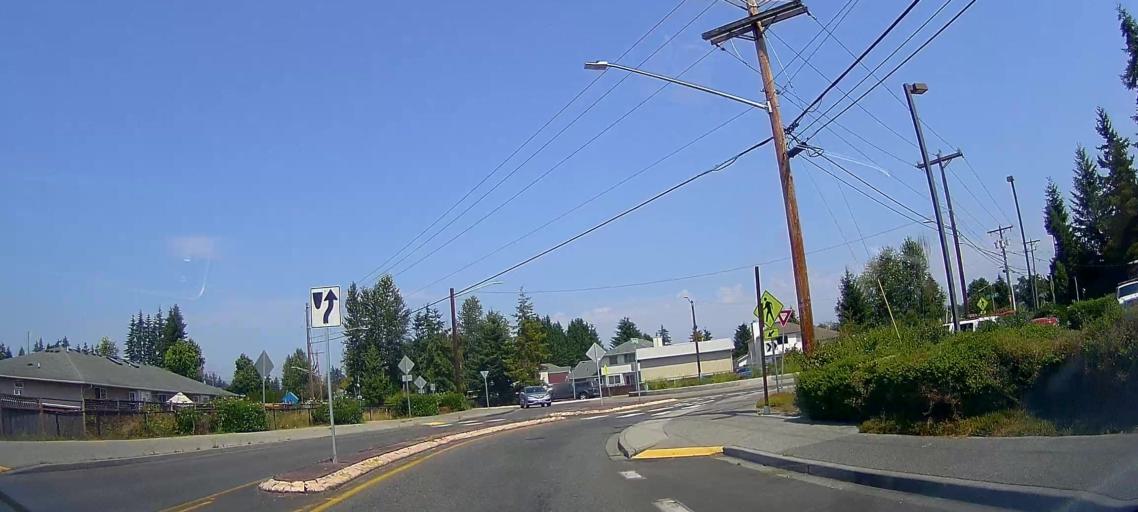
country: US
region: Washington
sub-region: Snohomish County
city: Marysville
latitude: 48.0921
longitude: -122.1626
